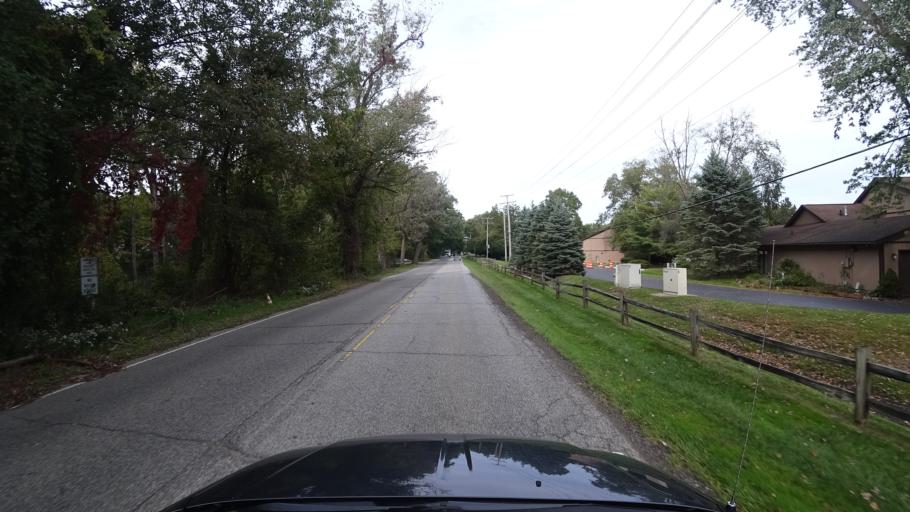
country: US
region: Indiana
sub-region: LaPorte County
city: Long Beach
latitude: 41.7369
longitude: -86.8557
